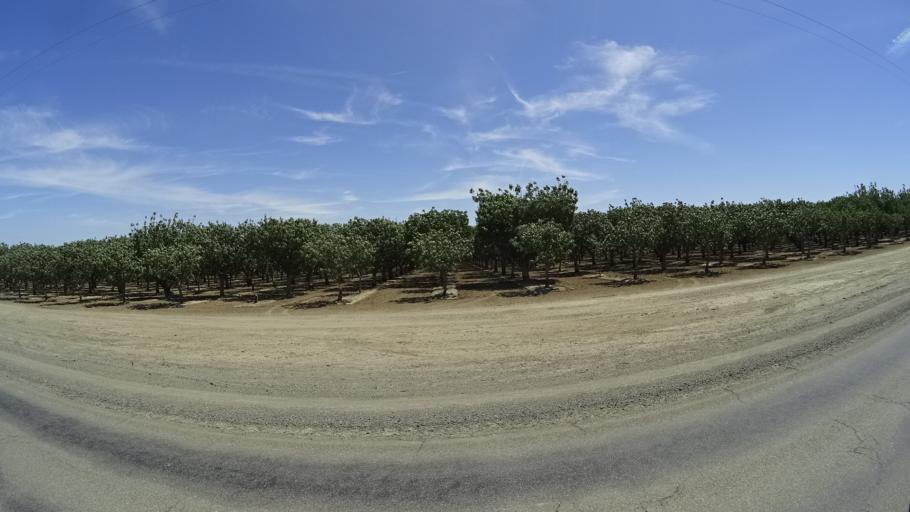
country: US
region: California
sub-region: Kings County
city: Kettleman City
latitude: 35.9180
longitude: -119.9150
